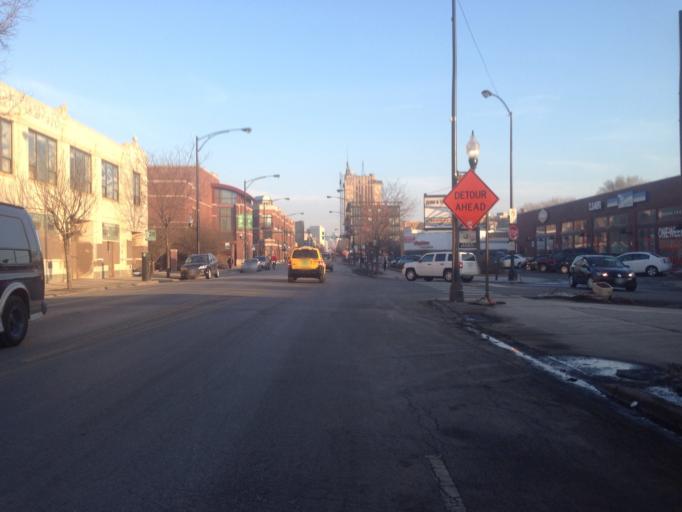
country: US
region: Illinois
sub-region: Cook County
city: Chicago
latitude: 41.9129
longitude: -87.6815
